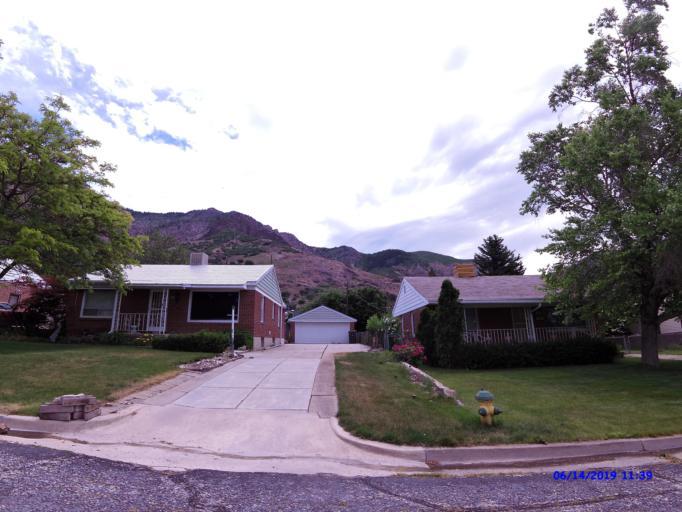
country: US
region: Utah
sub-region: Weber County
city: Ogden
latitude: 41.2511
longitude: -111.9410
